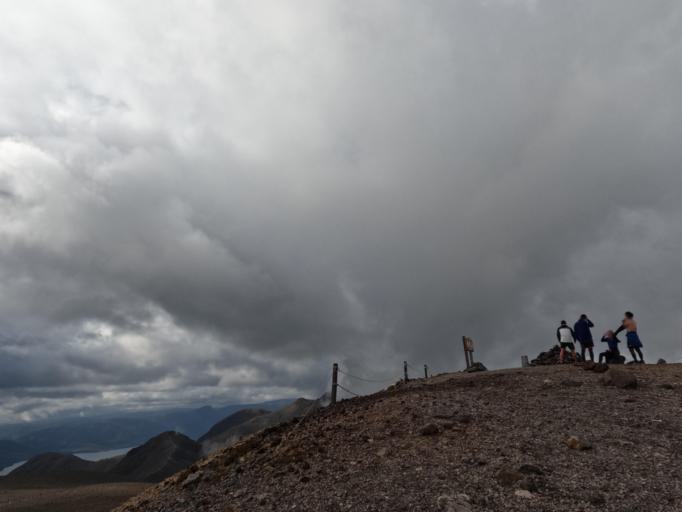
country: JP
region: Hokkaido
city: Shiraoi
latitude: 42.6918
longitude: 141.3867
